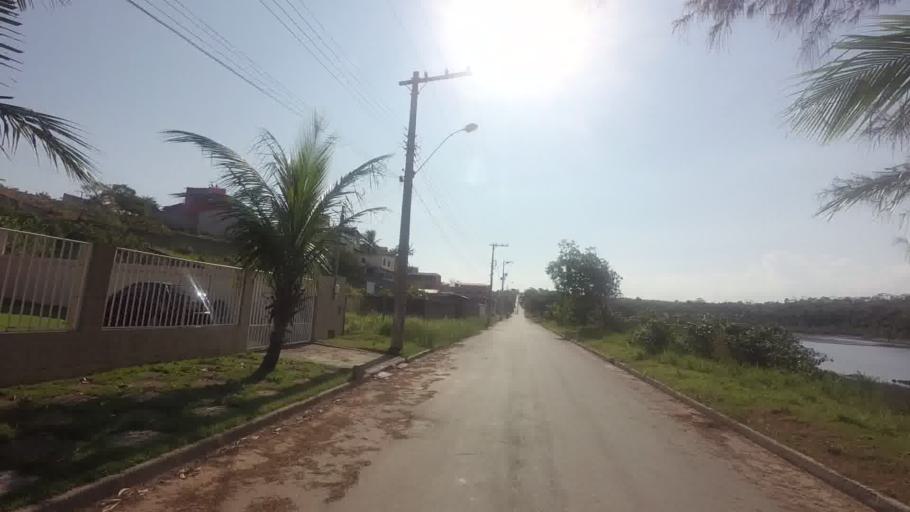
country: BR
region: Espirito Santo
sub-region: Guarapari
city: Guarapari
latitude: -20.7202
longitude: -40.5260
